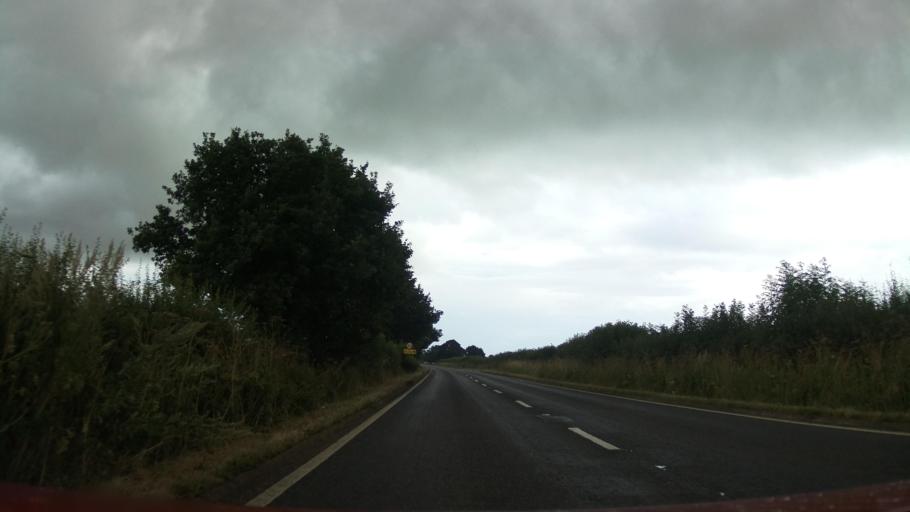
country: GB
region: England
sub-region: Oxfordshire
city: Hanwell
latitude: 52.1190
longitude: -1.3505
